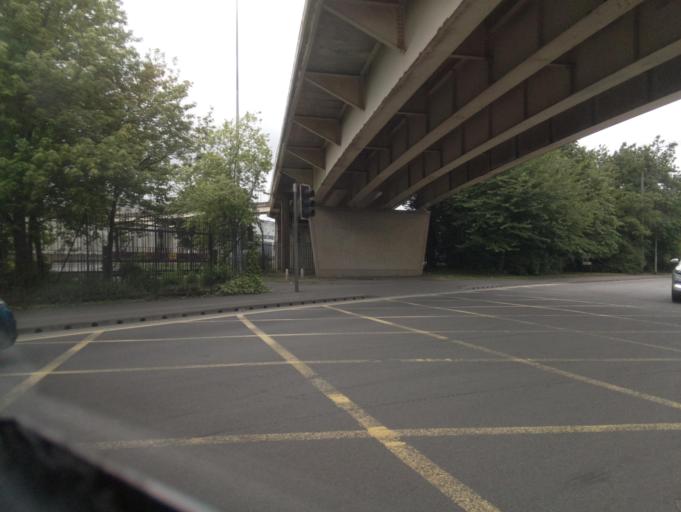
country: GB
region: England
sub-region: Staffordshire
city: Burton upon Trent
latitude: 52.8089
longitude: -1.6330
